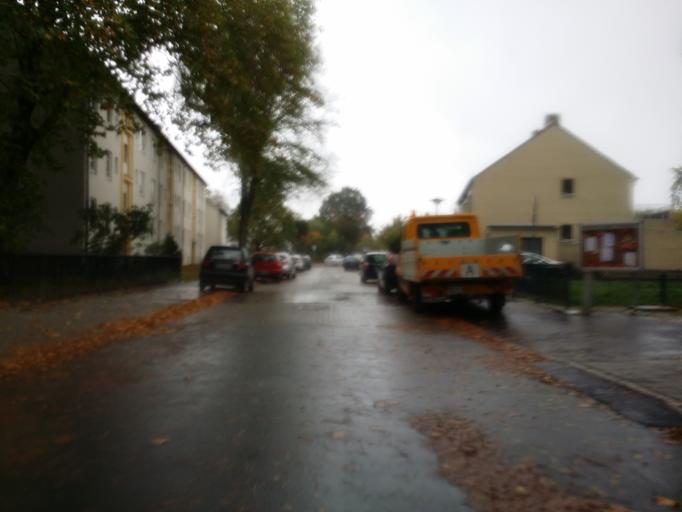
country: DE
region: Bremen
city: Bremen
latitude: 53.0333
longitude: 8.8132
